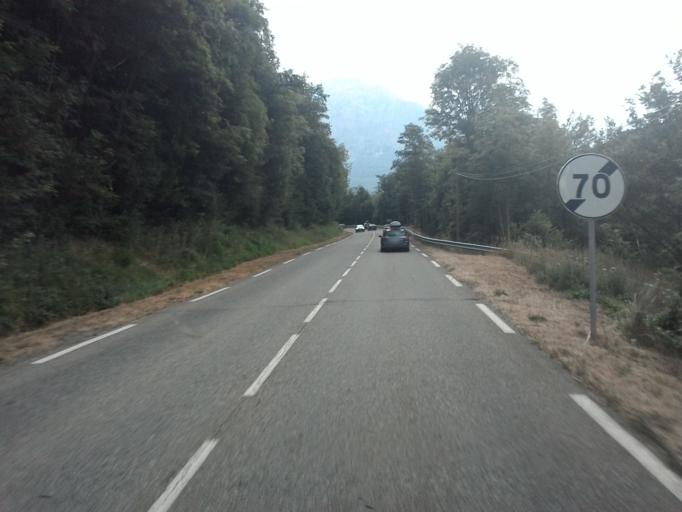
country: FR
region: Provence-Alpes-Cote d'Azur
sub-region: Departement des Hautes-Alpes
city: Saint-Bonnet-en-Champsaur
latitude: 44.7771
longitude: 5.9891
